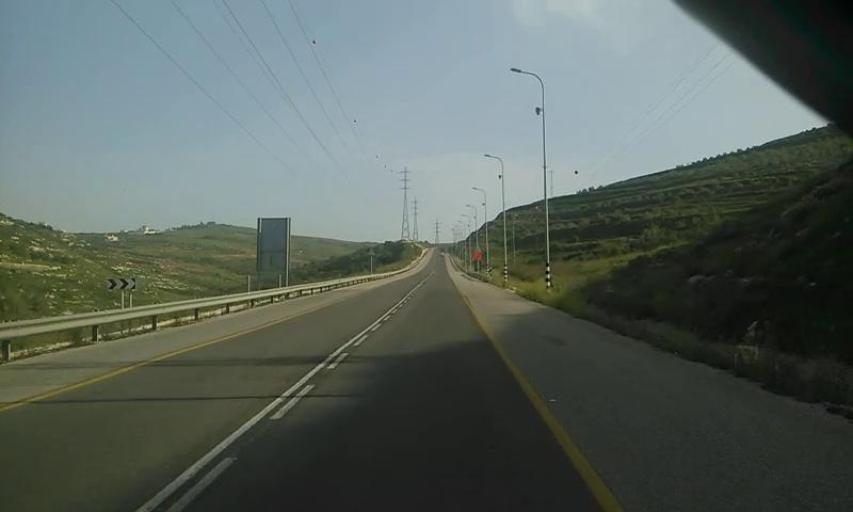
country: PS
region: West Bank
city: Jit
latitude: 32.2115
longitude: 35.1808
